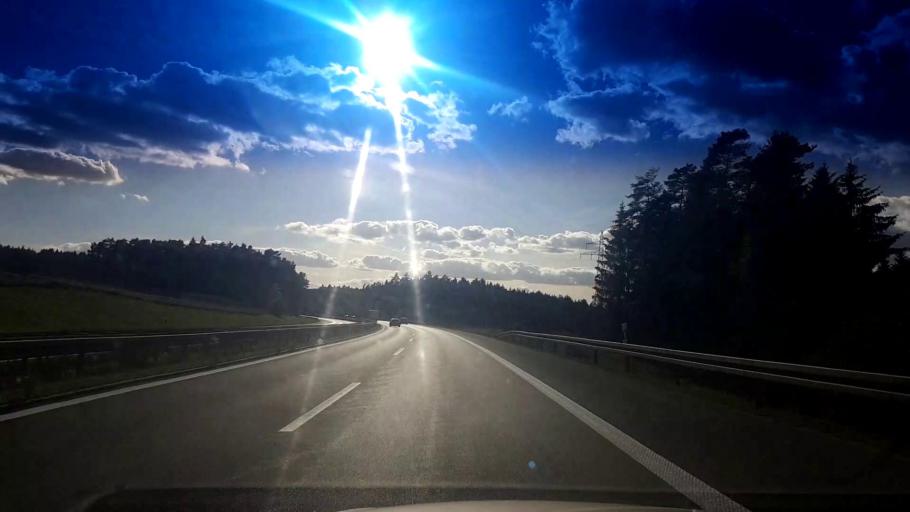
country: DE
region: Bavaria
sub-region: Upper Franconia
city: Stadelhofen
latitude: 50.0087
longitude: 11.2331
